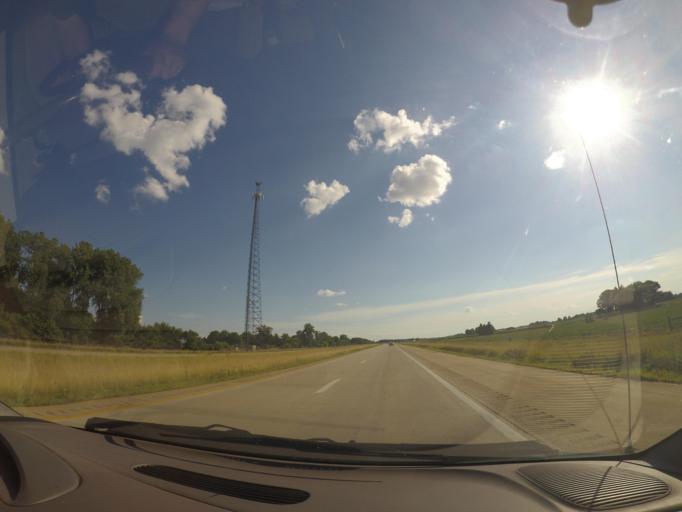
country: US
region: Ohio
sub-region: Lucas County
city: Whitehouse
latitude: 41.4636
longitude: -83.7851
